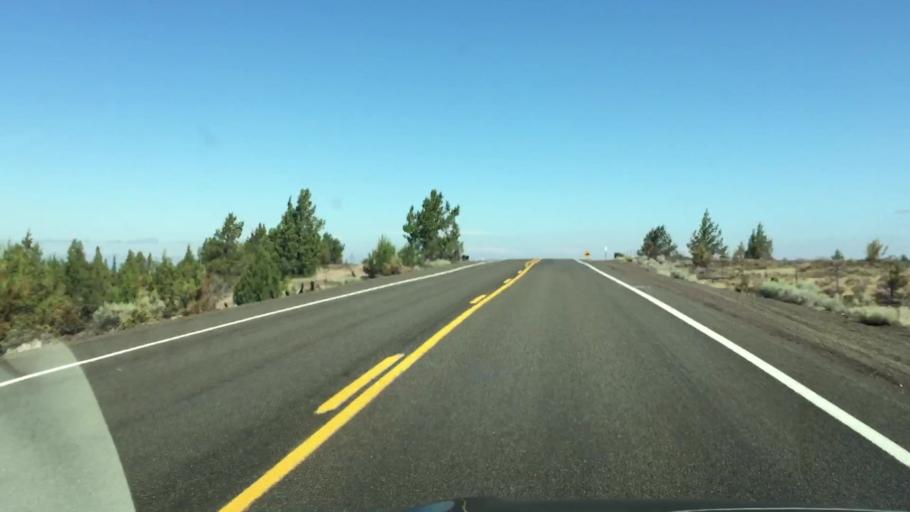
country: US
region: Oregon
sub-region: Jefferson County
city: Warm Springs
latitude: 45.0833
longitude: -121.0259
